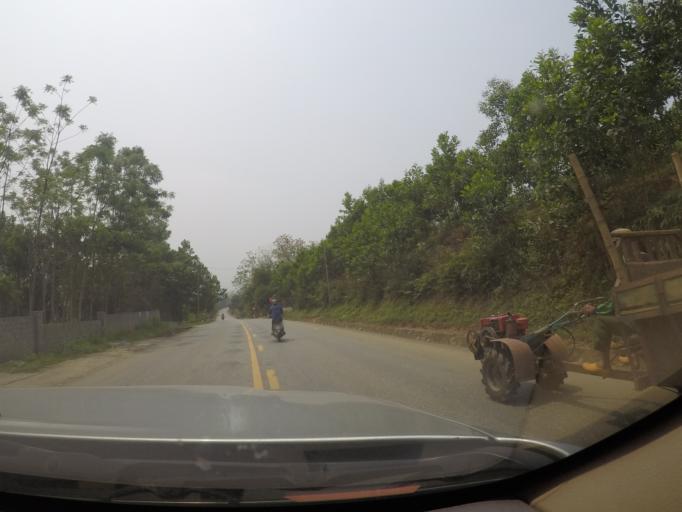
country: VN
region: Thanh Hoa
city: Thi Tran Ngoc Lac
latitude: 20.1349
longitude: 105.4148
